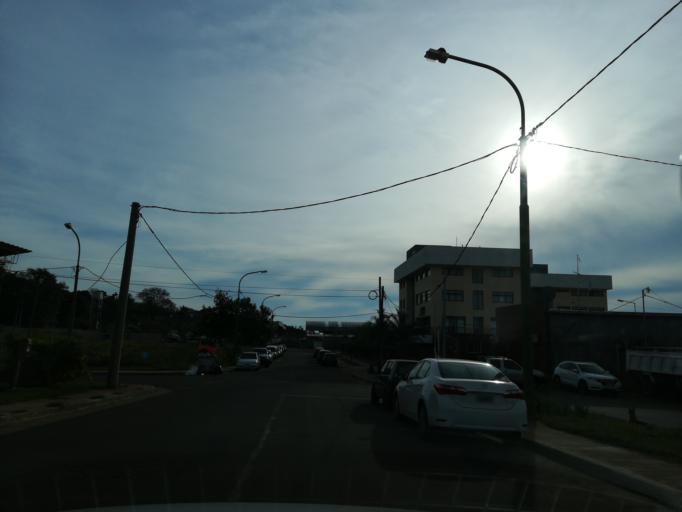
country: AR
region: Misiones
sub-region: Departamento de Capital
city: Posadas
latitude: -27.3548
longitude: -55.9136
